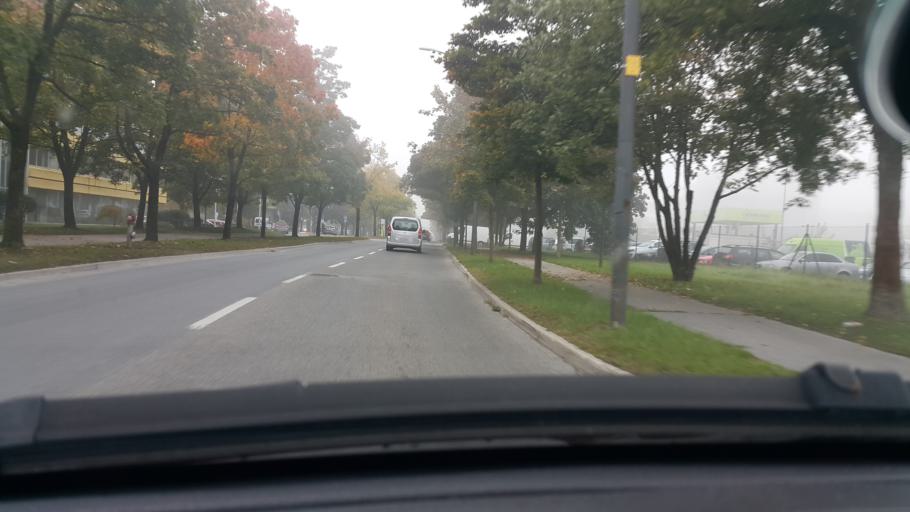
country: SI
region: Ljubljana
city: Ljubljana
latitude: 46.0816
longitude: 14.5019
